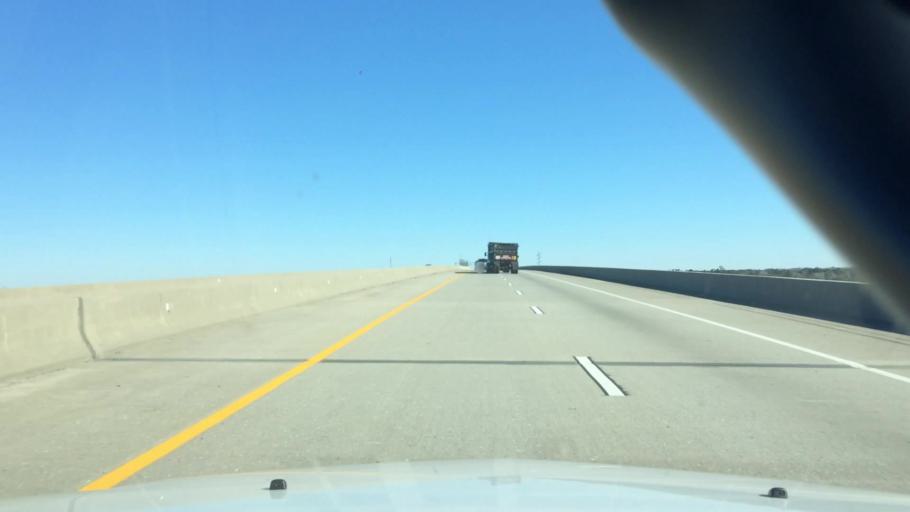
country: US
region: North Carolina
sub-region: New Hanover County
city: Wrightsboro
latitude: 34.2972
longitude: -77.9611
